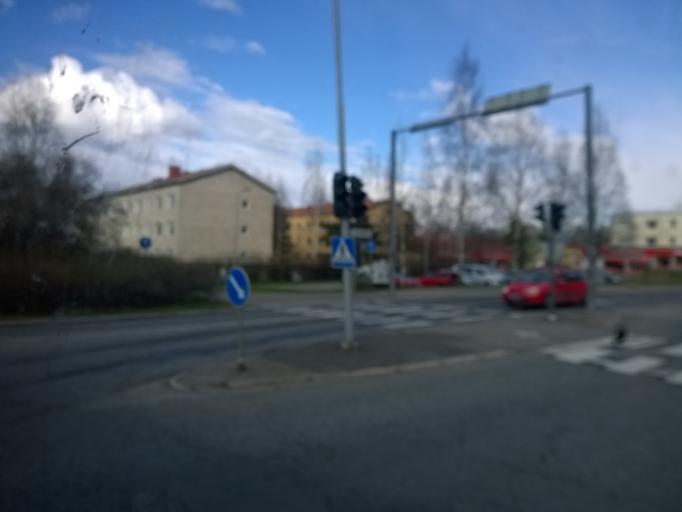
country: FI
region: Pirkanmaa
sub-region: Tampere
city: Tampere
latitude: 61.4721
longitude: 23.7747
